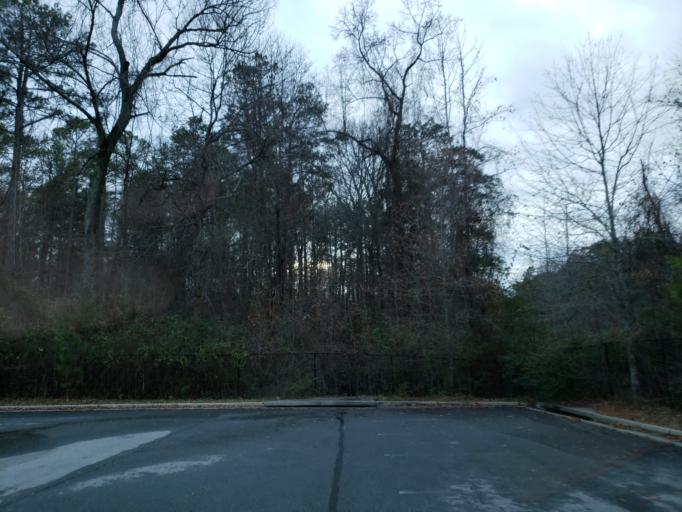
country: US
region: Georgia
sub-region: Cobb County
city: Marietta
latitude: 33.9850
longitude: -84.5835
